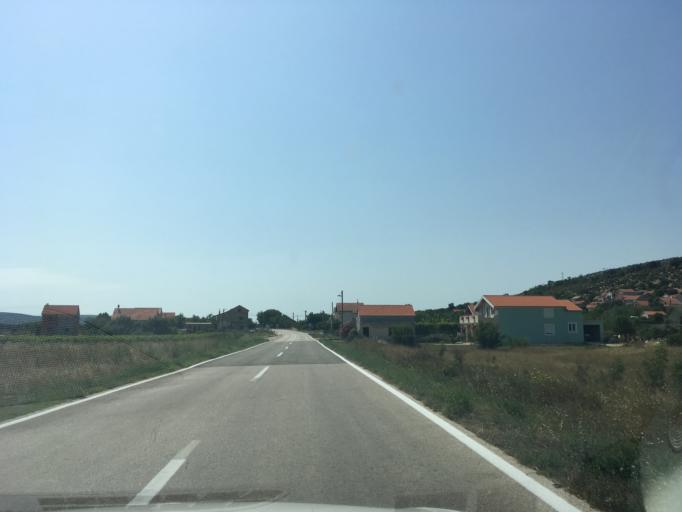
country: HR
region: Zadarska
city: Benkovac
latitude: 43.9637
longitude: 15.7550
